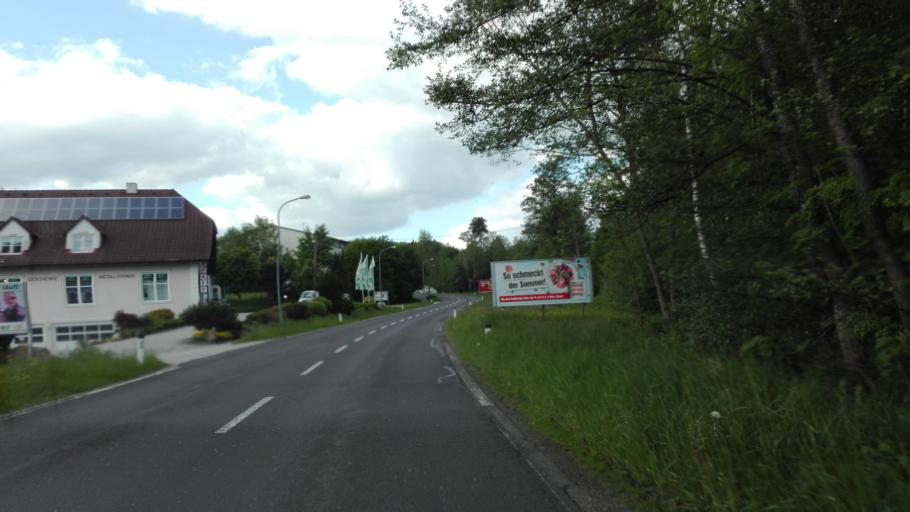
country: AT
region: Upper Austria
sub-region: Politischer Bezirk Perg
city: Bad Kreuzen
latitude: 48.3942
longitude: 14.7308
